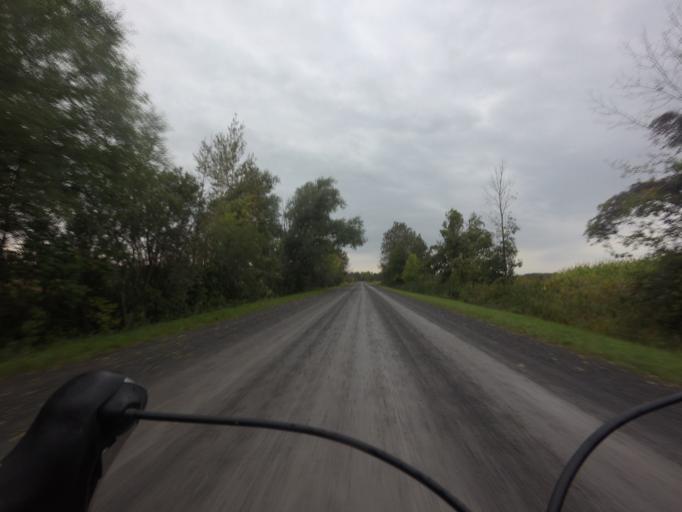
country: CA
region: Ontario
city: Bells Corners
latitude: 45.1670
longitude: -75.6837
